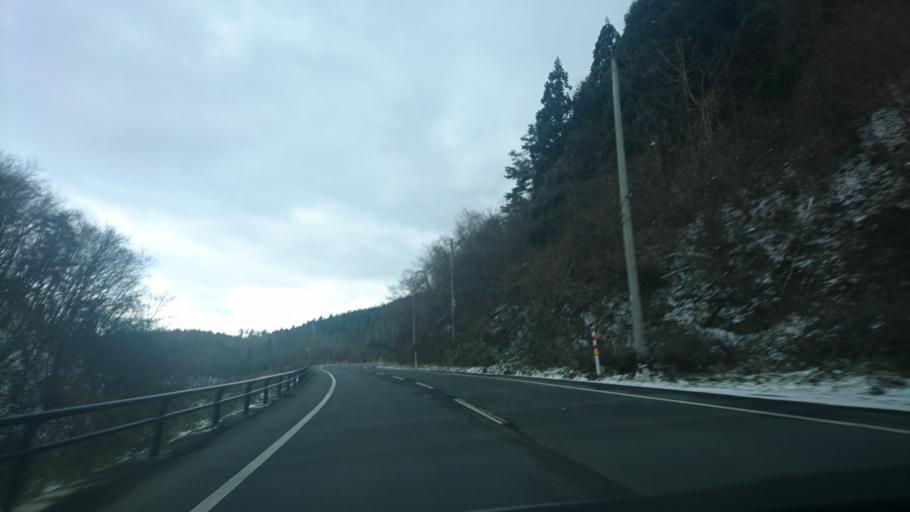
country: JP
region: Iwate
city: Mizusawa
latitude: 39.1644
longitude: 141.2506
